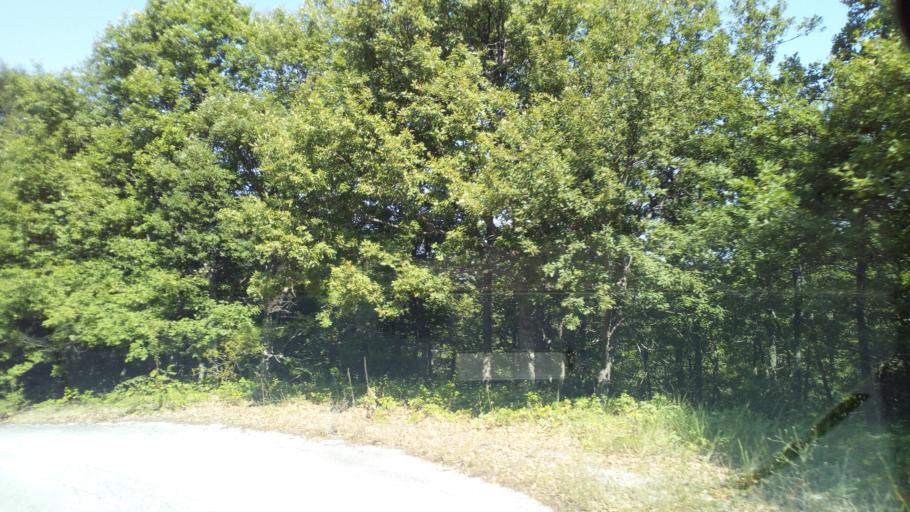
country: GR
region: Central Macedonia
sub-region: Nomos Thessalonikis
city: Sochos
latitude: 40.8304
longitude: 23.3559
